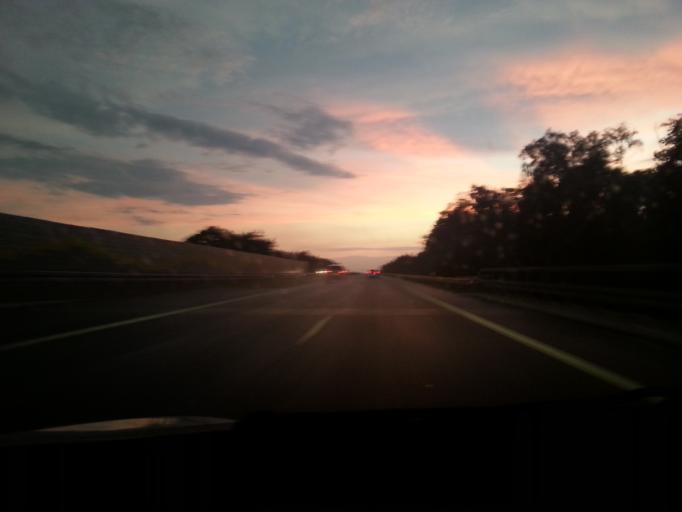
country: PL
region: Lodz Voivodeship
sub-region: Powiat zdunskowolski
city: Zdunska Wola
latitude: 51.5710
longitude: 18.9627
